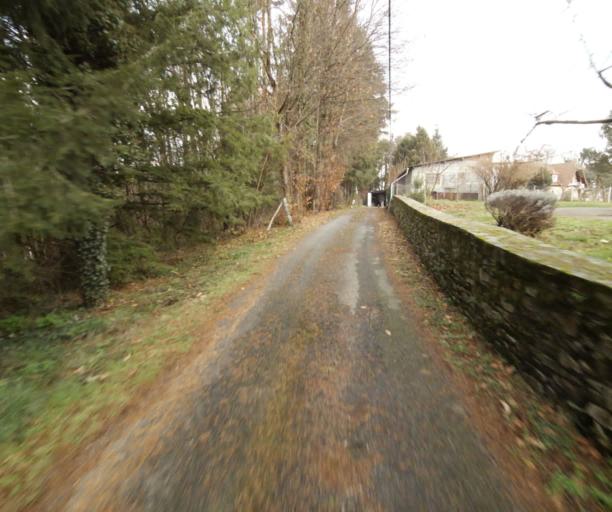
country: FR
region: Limousin
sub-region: Departement de la Correze
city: Chameyrat
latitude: 45.2327
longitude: 1.7027
